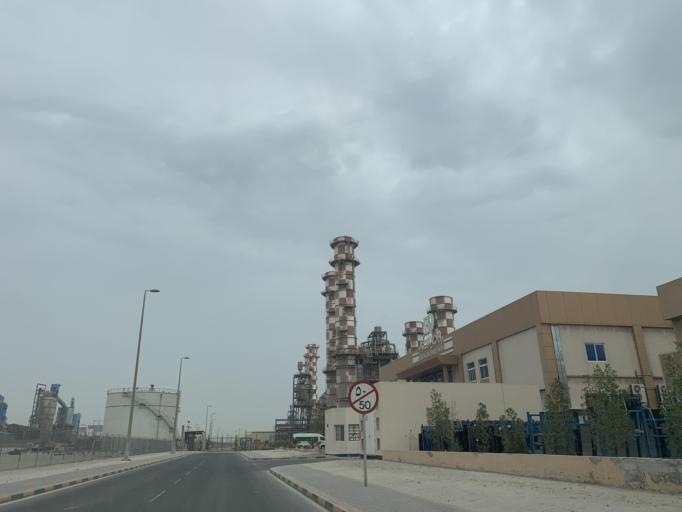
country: BH
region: Muharraq
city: Al Hadd
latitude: 26.2150
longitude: 50.6589
